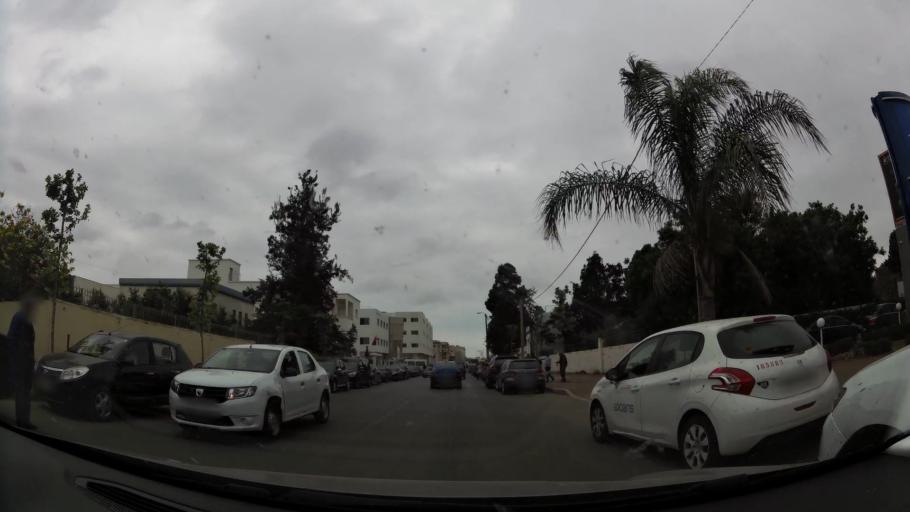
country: MA
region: Rabat-Sale-Zemmour-Zaer
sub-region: Rabat
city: Rabat
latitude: 33.9750
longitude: -6.8176
